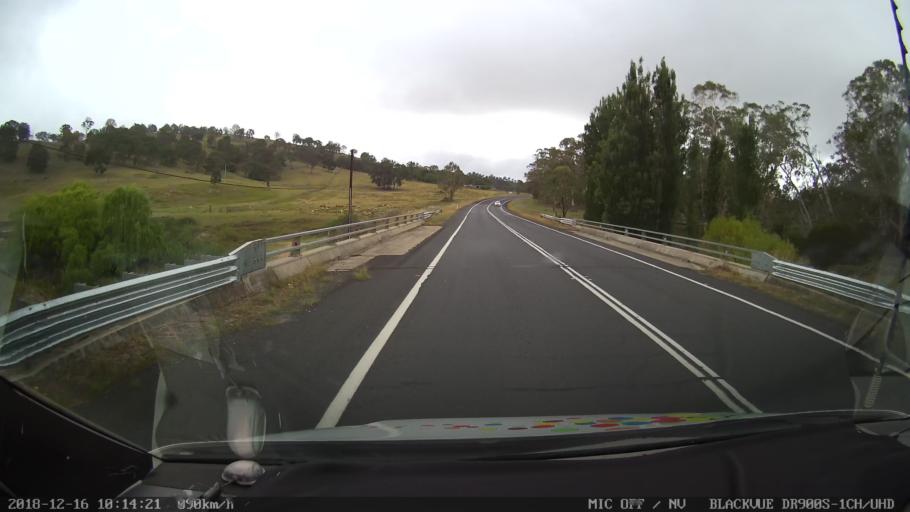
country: AU
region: New South Wales
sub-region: Tenterfield Municipality
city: Carrolls Creek
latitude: -29.2878
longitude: 151.9621
